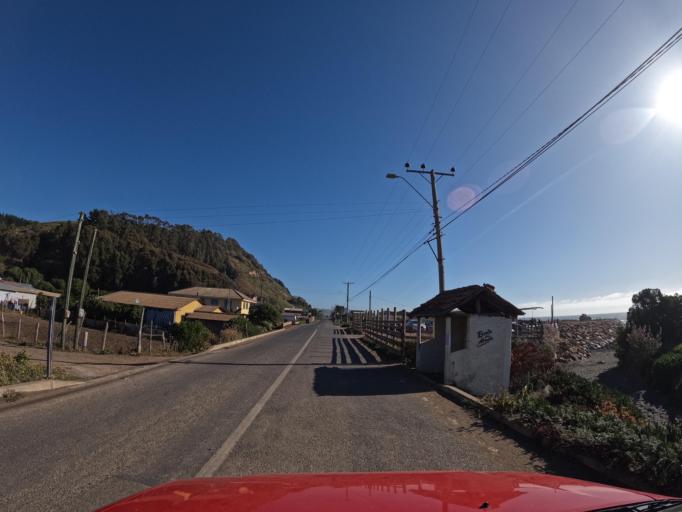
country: CL
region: Maule
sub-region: Provincia de Talca
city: Constitucion
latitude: -34.8558
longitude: -72.1446
